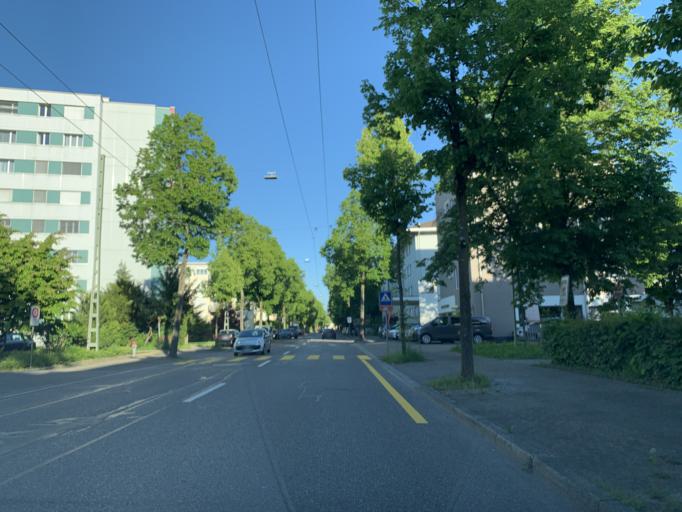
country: CH
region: Zurich
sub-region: Bezirk Winterthur
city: Mattenbach (Kreis 7) / Endliker
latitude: 47.4892
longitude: 8.7505
